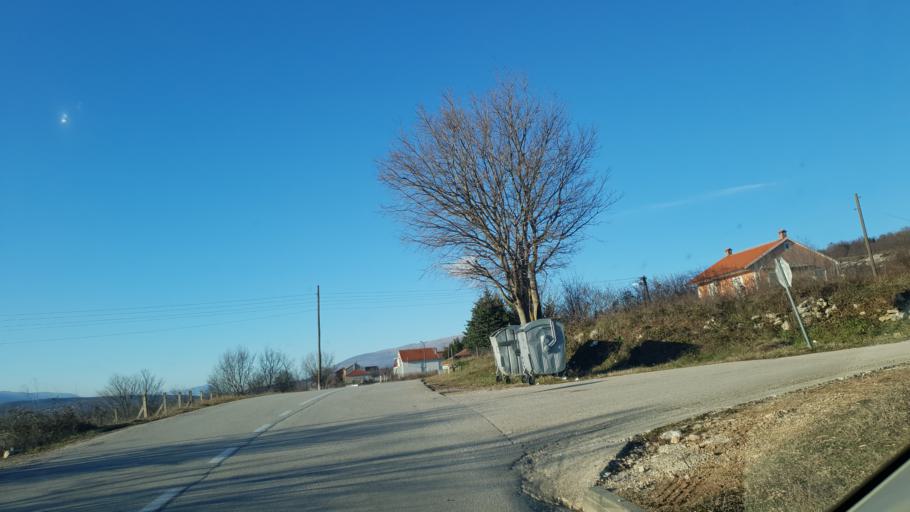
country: HR
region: Splitsko-Dalmatinska
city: Gala
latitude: 43.7373
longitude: 16.6826
